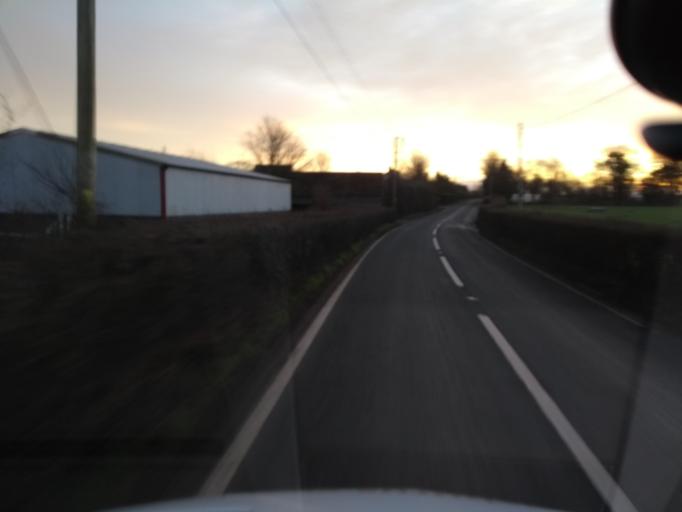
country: GB
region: England
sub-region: Somerset
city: Wedmore
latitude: 51.2267
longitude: -2.8820
